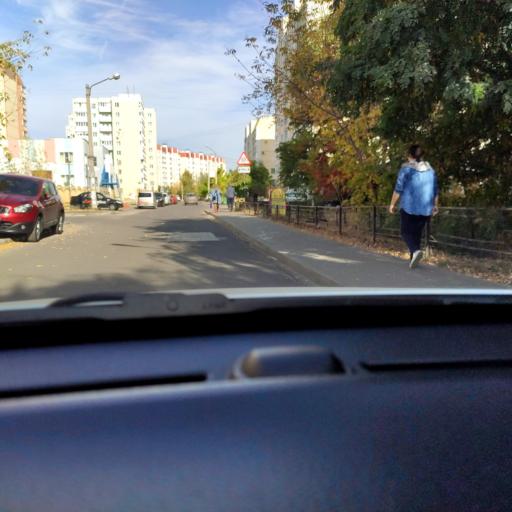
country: RU
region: Voronezj
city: Podgornoye
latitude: 51.7278
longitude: 39.2044
